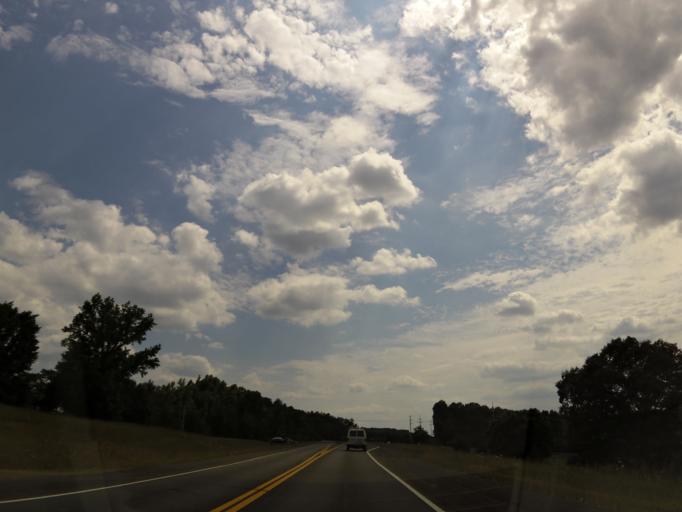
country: US
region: Tennessee
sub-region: Marion County
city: Whitwell
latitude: 35.1379
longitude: -85.5488
